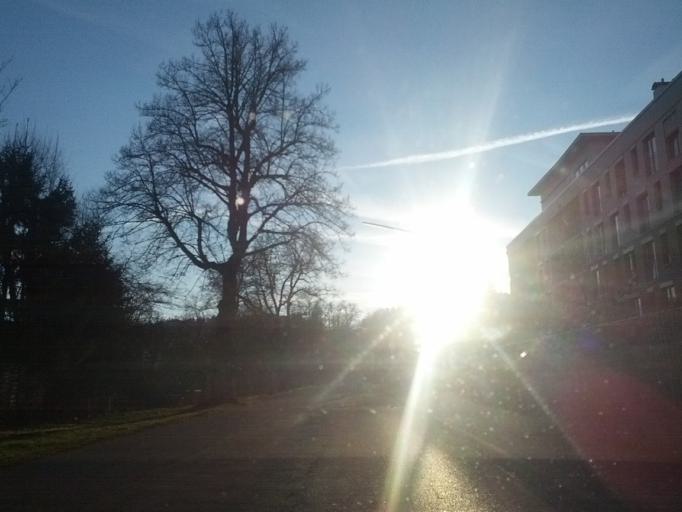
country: DE
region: Bavaria
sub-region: Swabia
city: Ottobeuren
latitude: 47.9371
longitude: 10.2950
